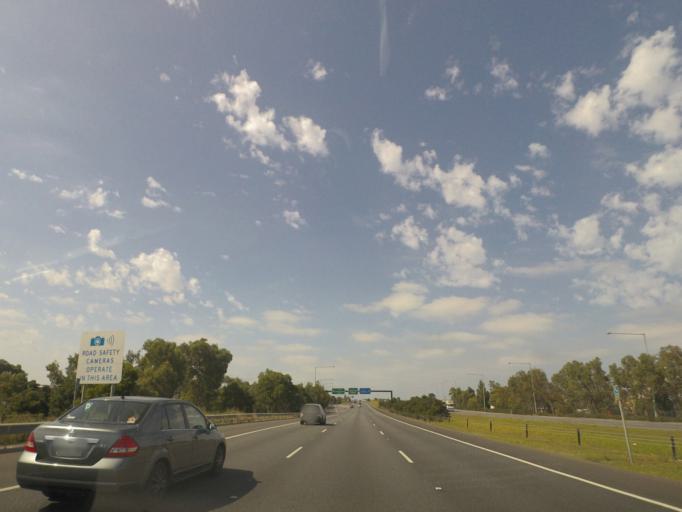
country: AU
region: Victoria
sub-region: Greater Dandenong
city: Dandenong
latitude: -37.9862
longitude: 145.1935
